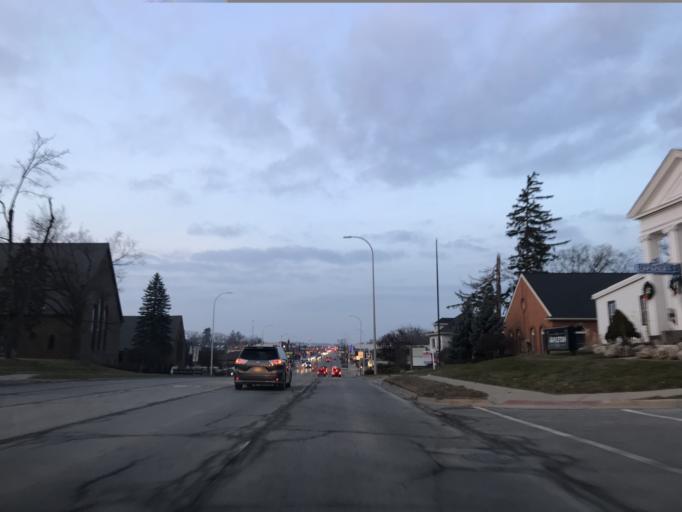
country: US
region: Michigan
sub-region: Livingston County
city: Brighton
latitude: 42.5269
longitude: -83.7788
